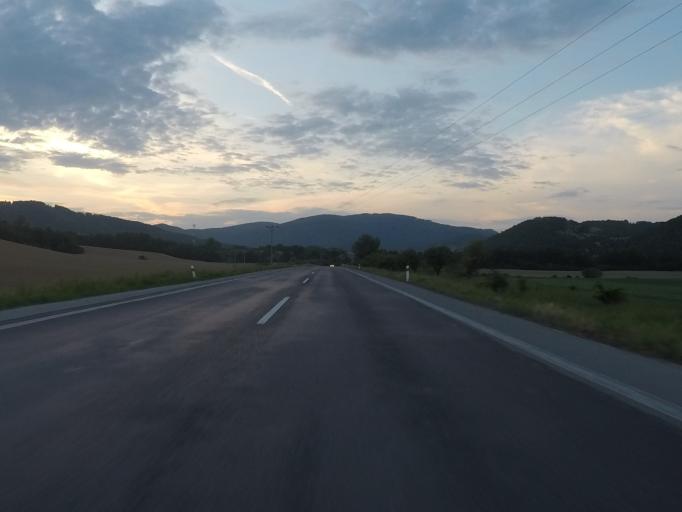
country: SK
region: Banskobystricky
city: Rimavska Sobota
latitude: 48.4874
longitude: 19.9434
